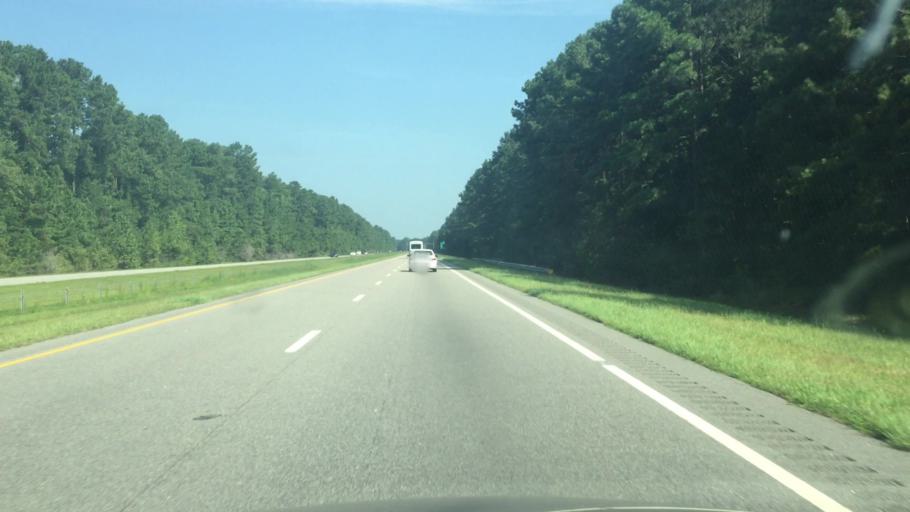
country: US
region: North Carolina
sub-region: Robeson County
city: Lumberton
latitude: 34.5513
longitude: -79.0236
